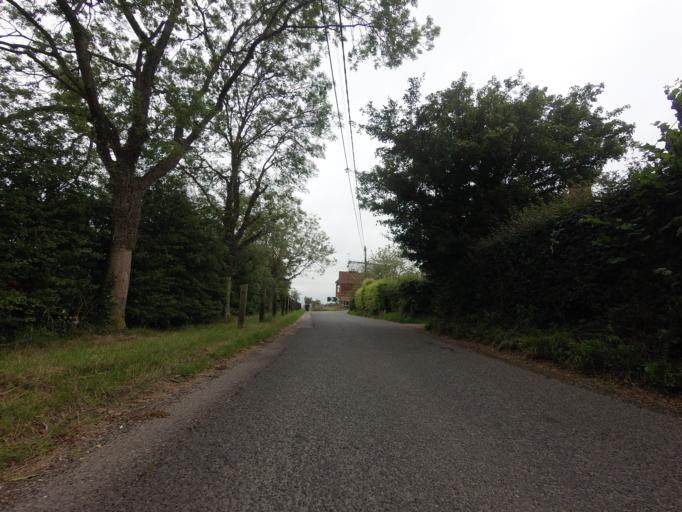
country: GB
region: England
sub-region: Kent
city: Borough Green
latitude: 51.3069
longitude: 0.2694
